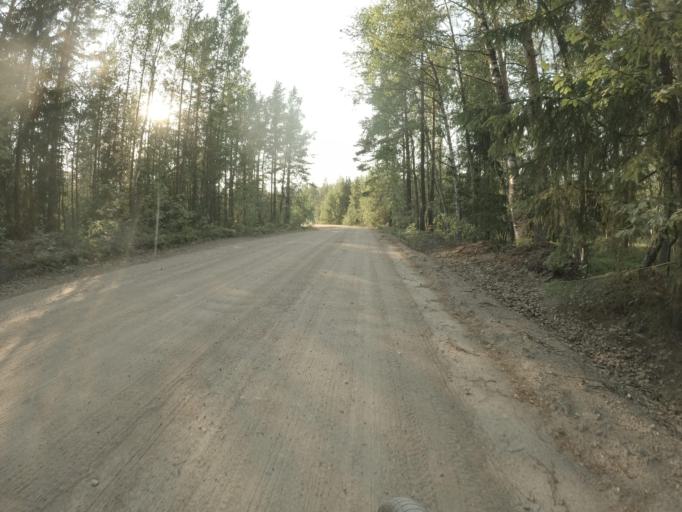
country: RU
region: Leningrad
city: Veshchevo
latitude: 60.4614
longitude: 29.2420
